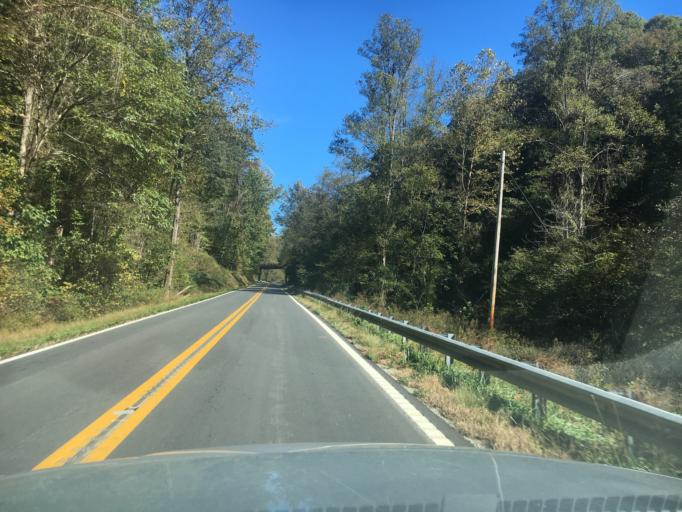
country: US
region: North Carolina
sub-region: Burke County
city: Glen Alpine
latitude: 35.5716
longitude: -81.8472
